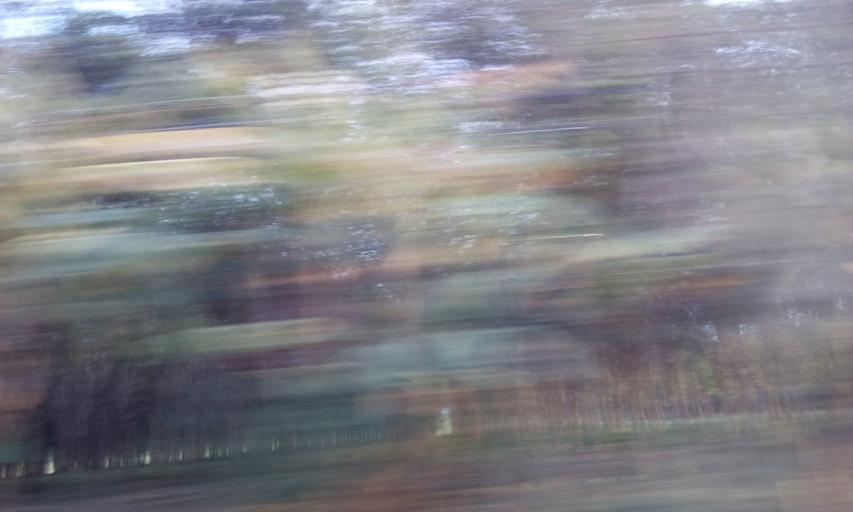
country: TH
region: Trat
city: Laem Ngop
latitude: 12.2626
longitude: 102.2951
